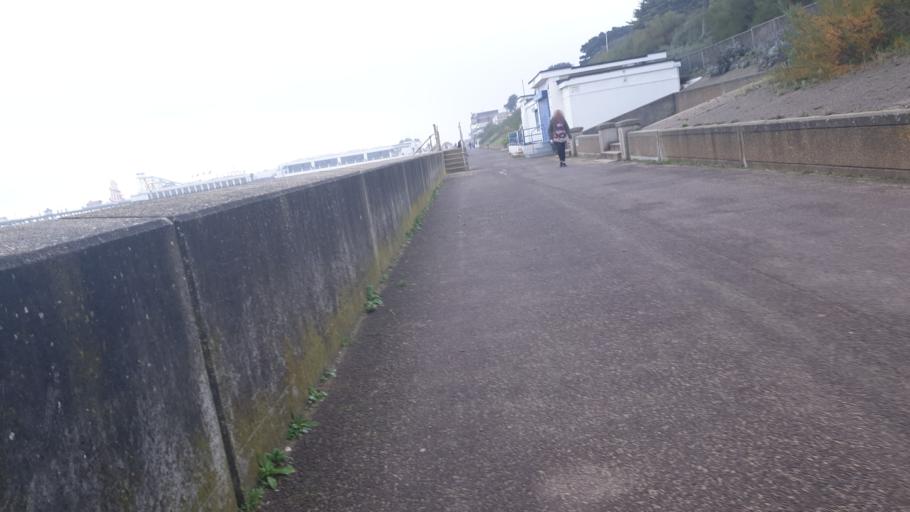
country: GB
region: England
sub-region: Essex
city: Clacton-on-Sea
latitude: 51.7889
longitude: 1.1594
